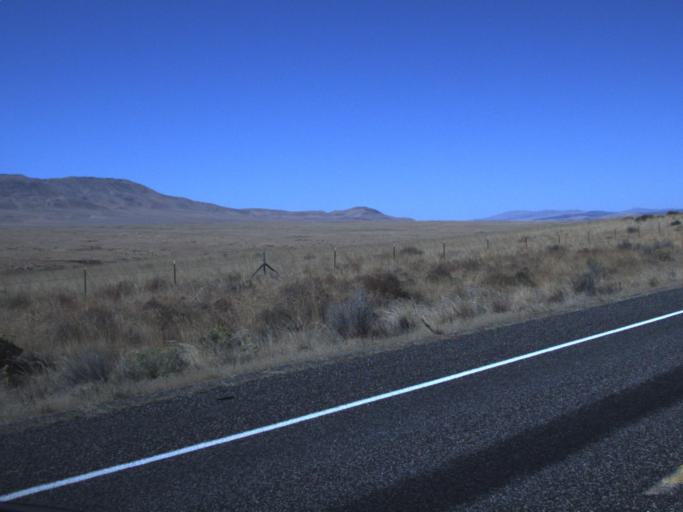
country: US
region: Washington
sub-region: Benton County
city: West Richland
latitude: 46.4191
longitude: -119.4635
